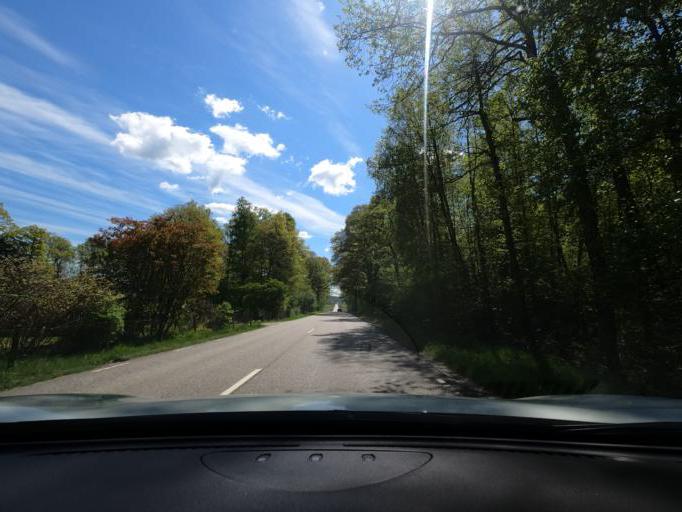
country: SE
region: Halland
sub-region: Kungsbacka Kommun
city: Fjaeras kyrkby
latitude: 57.4330
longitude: 12.1832
